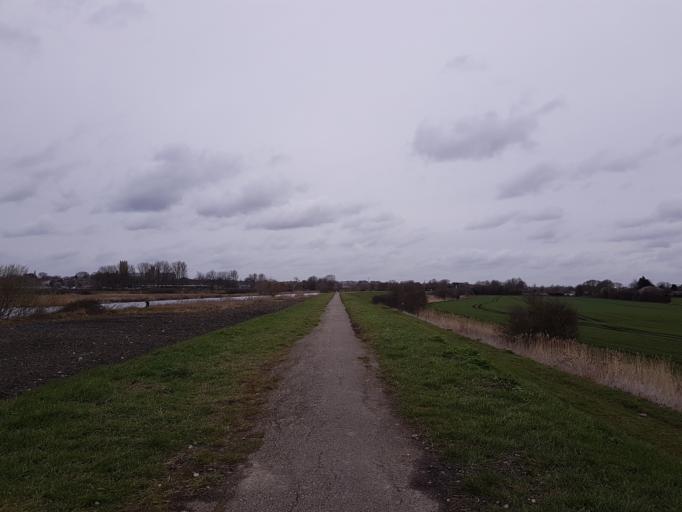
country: GB
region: England
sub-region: Cambridgeshire
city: Ely
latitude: 52.3847
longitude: 0.2672
